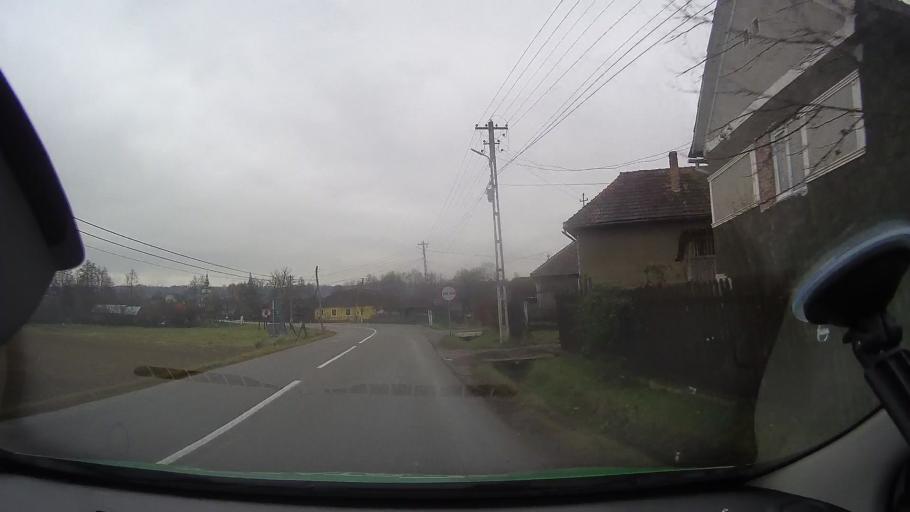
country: RO
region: Arad
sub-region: Comuna Varfurile
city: Varfurile
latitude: 46.3115
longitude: 22.5170
